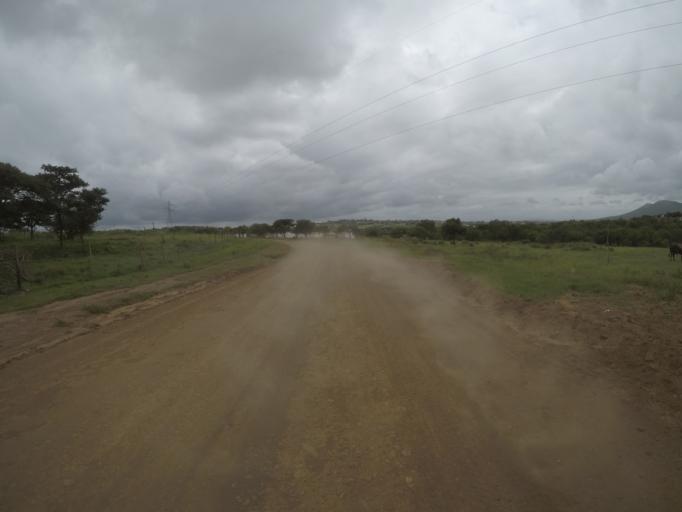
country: ZA
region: KwaZulu-Natal
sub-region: uThungulu District Municipality
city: Empangeni
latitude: -28.5931
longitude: 31.8409
